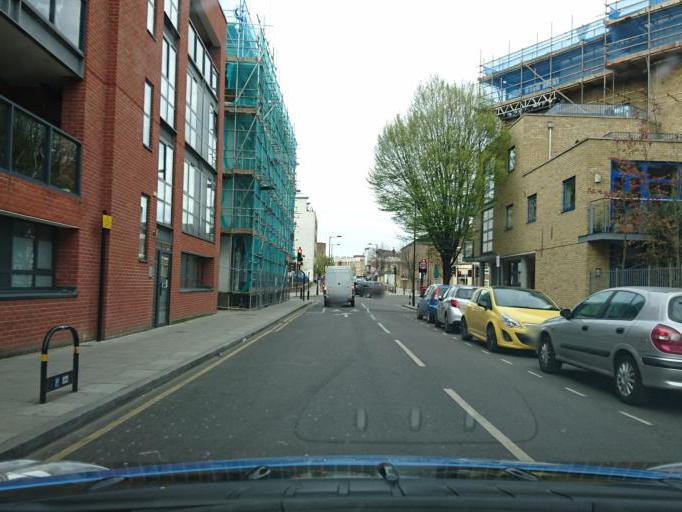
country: GB
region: England
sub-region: Greater London
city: Bethnal Green
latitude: 51.5345
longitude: -0.0636
